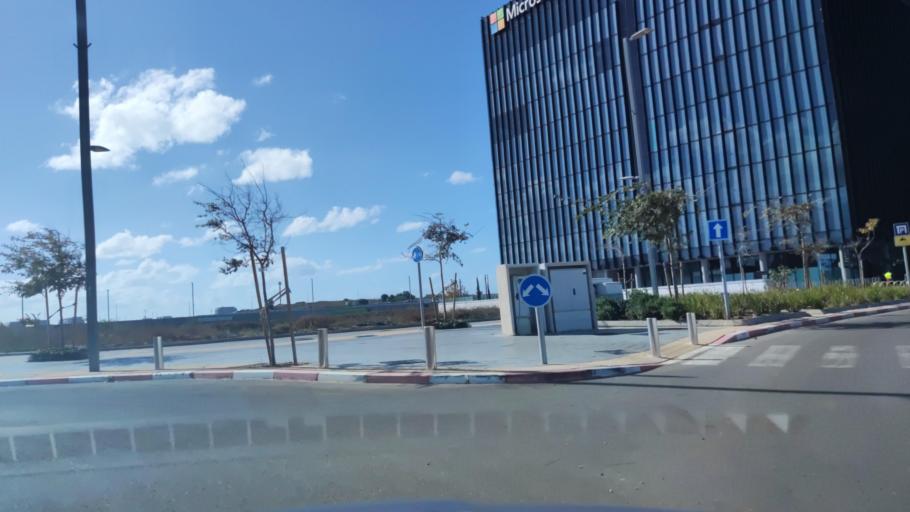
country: IL
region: Tel Aviv
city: Herzliya Pituah
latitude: 32.1568
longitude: 34.8070
